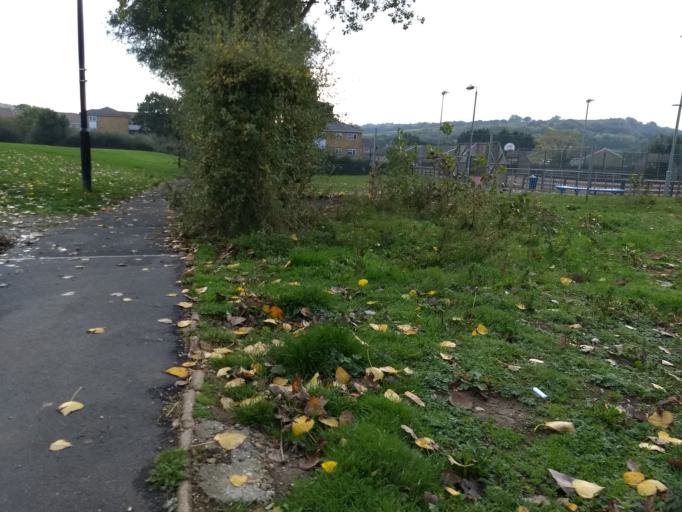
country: GB
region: England
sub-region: Isle of Wight
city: Newport
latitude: 50.6980
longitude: -1.2819
